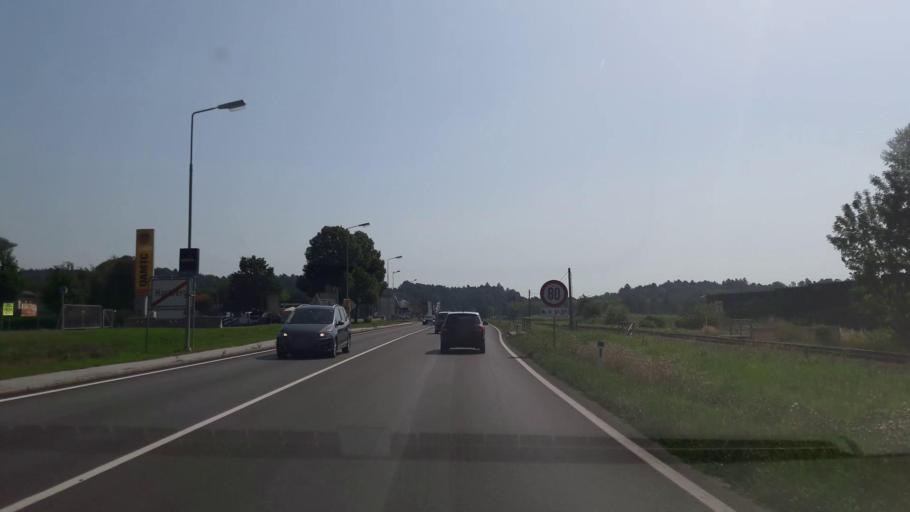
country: AT
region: Styria
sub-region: Politischer Bezirk Hartberg-Fuerstenfeld
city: Hartberg
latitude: 47.2833
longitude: 15.9927
